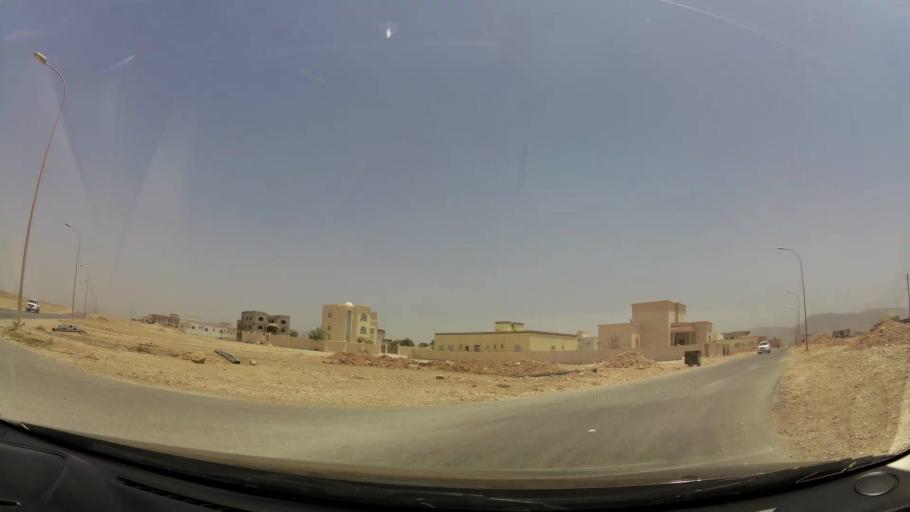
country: OM
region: Zufar
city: Salalah
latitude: 17.0917
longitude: 54.1838
